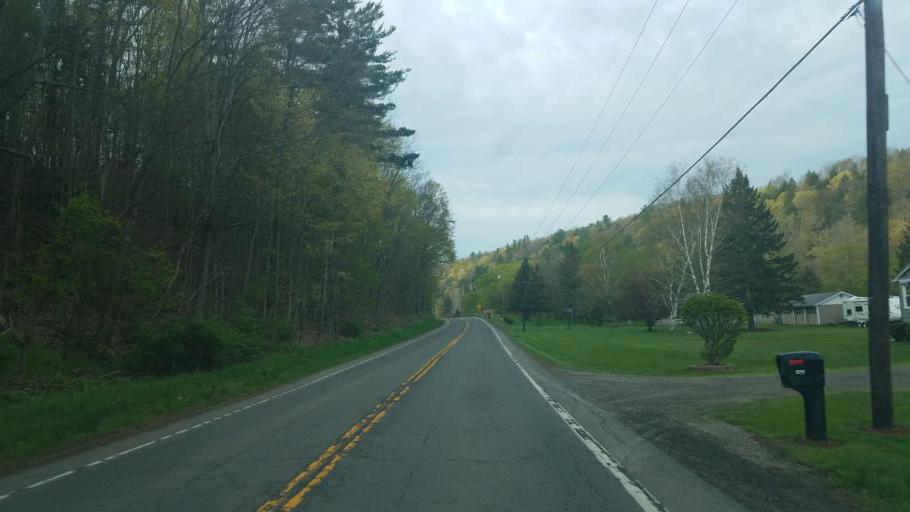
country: US
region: New York
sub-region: Steuben County
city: Canisteo
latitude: 42.2480
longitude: -77.5828
